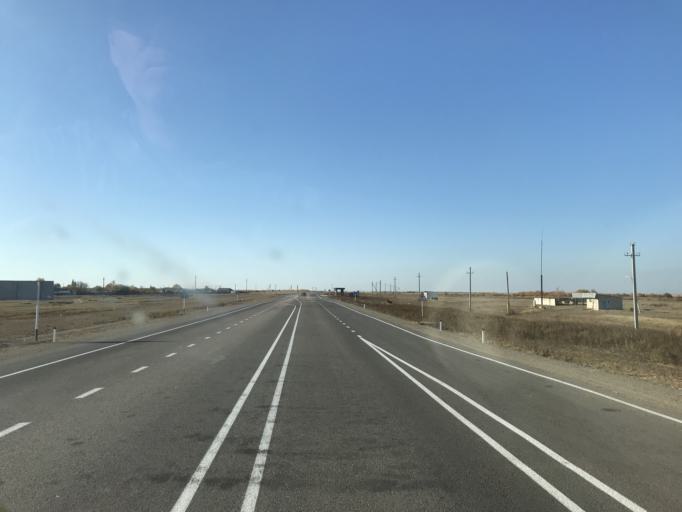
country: KZ
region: Pavlodar
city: Koktobe
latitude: 51.5044
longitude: 77.6976
